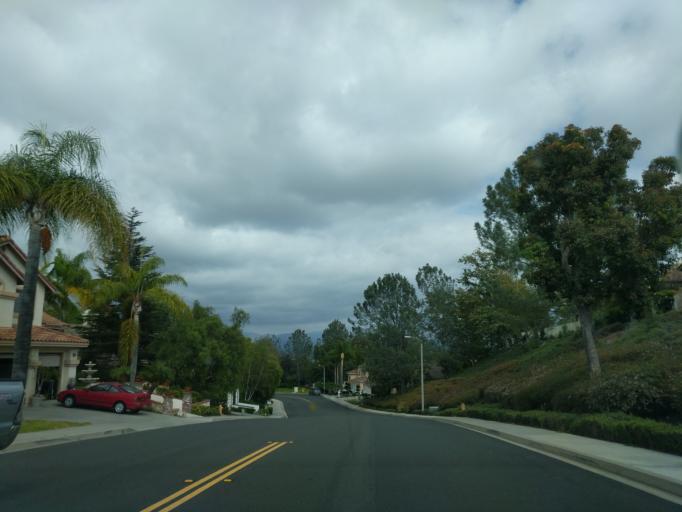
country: US
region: California
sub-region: Orange County
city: Laguna Woods
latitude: 33.5992
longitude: -117.7363
